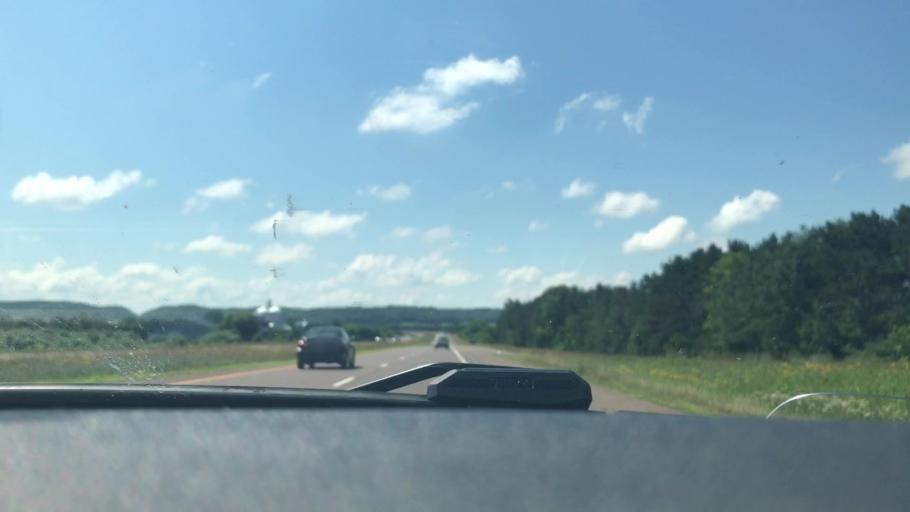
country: US
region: Wisconsin
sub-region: Chippewa County
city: Chippewa Falls
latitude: 44.9980
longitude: -91.4421
